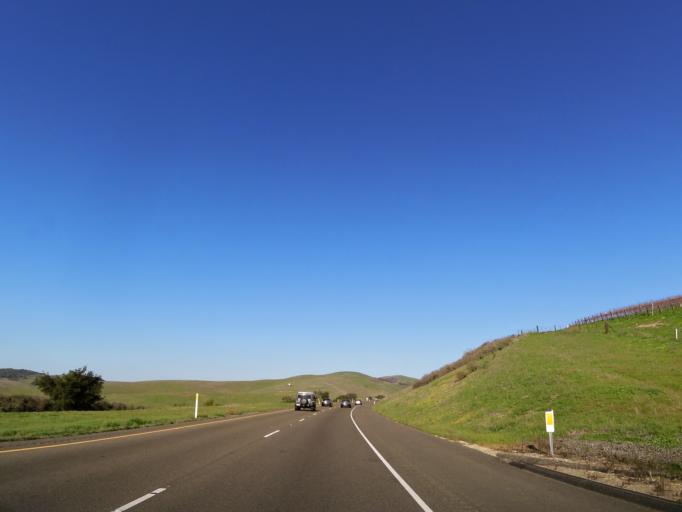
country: US
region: California
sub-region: Santa Barbara County
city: Los Alamos
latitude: 34.7936
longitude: -120.3359
